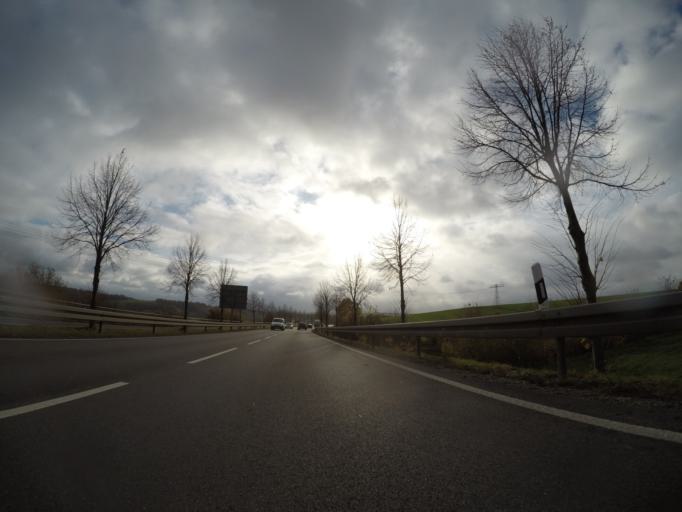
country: DE
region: Thuringia
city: Altenburg
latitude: 50.9610
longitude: 12.4307
